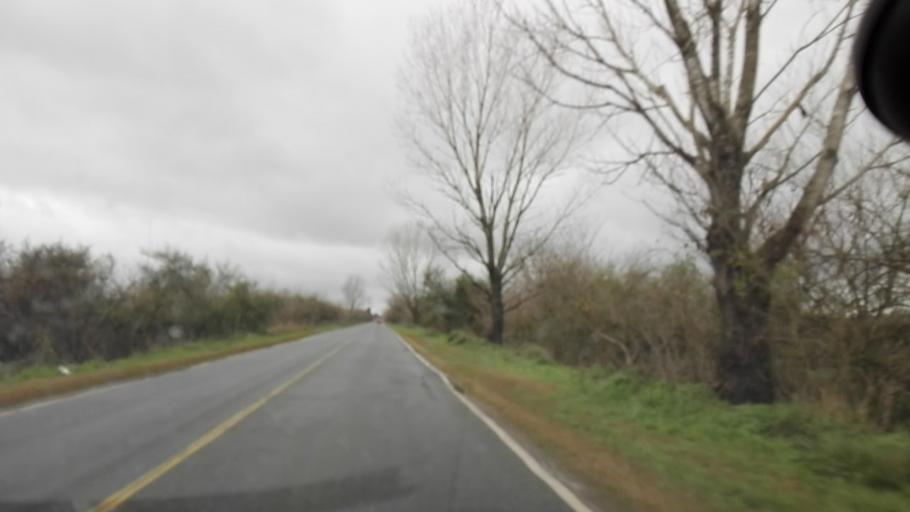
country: AR
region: Buenos Aires
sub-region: Partido de Brandsen
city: Brandsen
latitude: -35.1785
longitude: -58.2542
